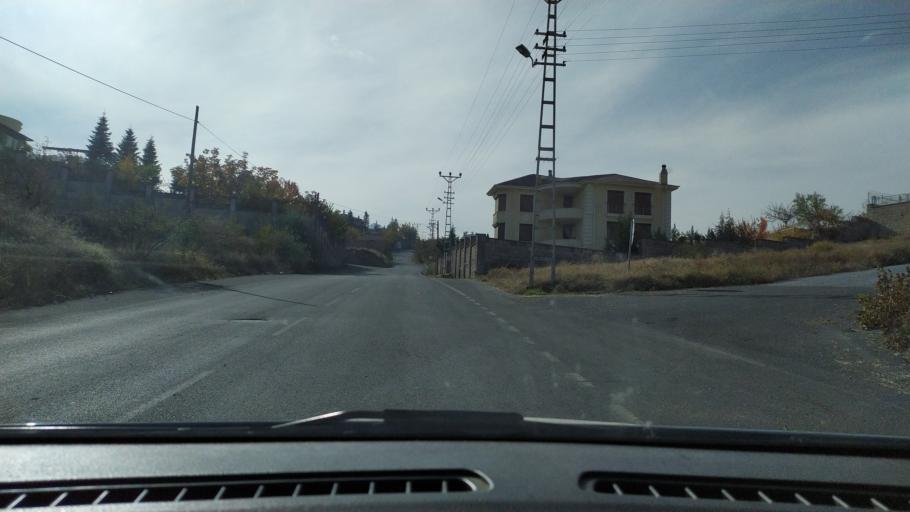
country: TR
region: Kayseri
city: Kayseri
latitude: 38.6800
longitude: 35.4913
